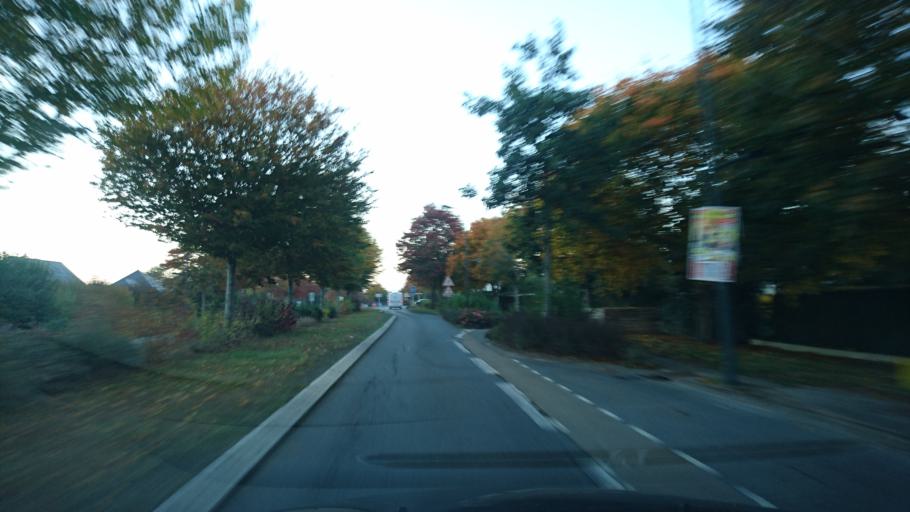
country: FR
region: Brittany
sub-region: Departement du Morbihan
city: Auray
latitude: 47.6796
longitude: -3.0120
